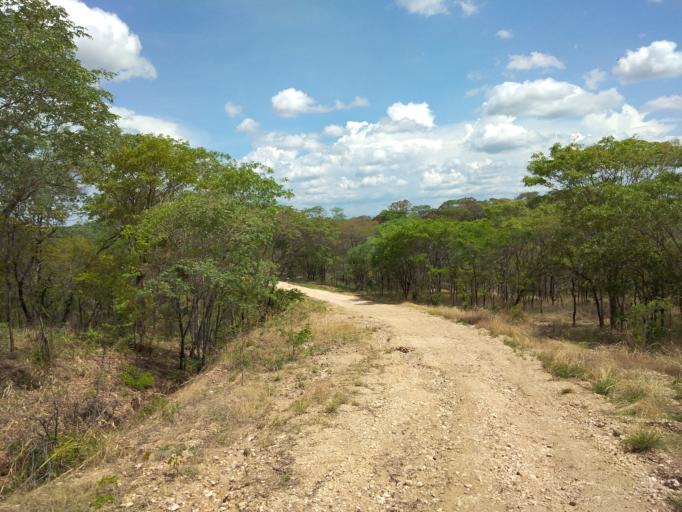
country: ZM
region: Central
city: Mkushi
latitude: -14.1147
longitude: 30.0082
